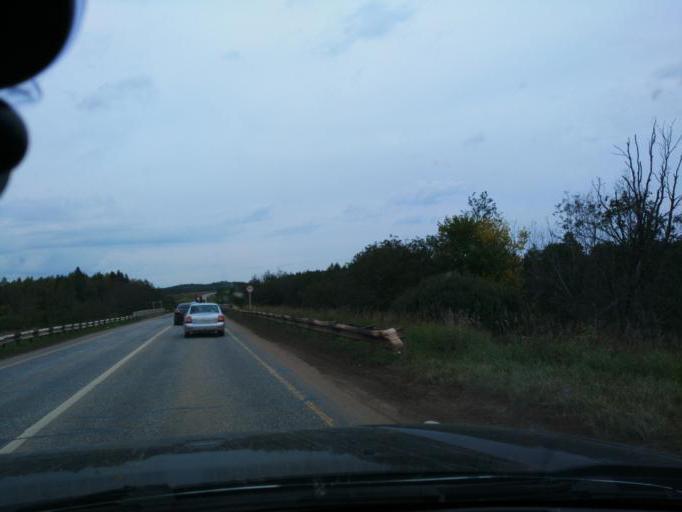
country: RU
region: Perm
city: Chernushka
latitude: 56.5602
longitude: 56.1145
